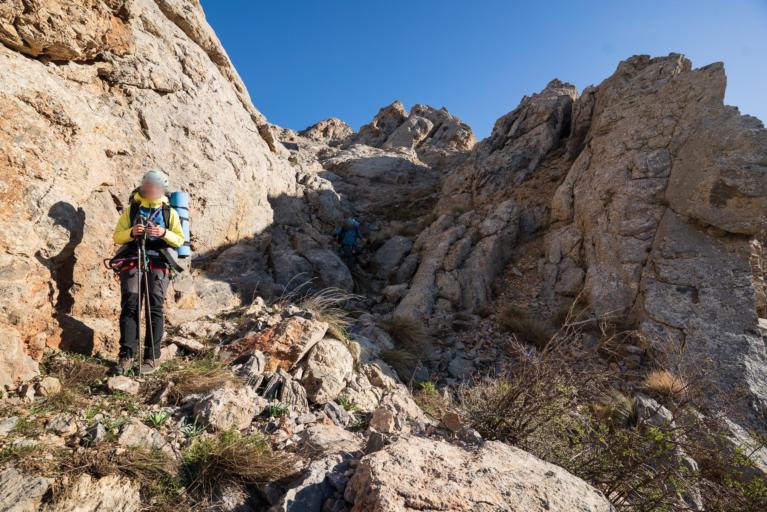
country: KZ
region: Ongtustik Qazaqstan
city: Ashchysay
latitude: 43.7642
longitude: 68.7785
